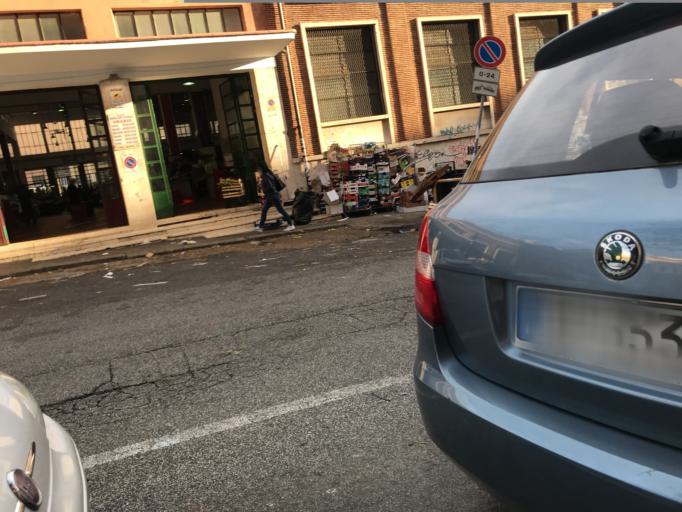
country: IT
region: Latium
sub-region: Citta metropolitana di Roma Capitale
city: Rome
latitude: 41.9091
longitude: 12.5190
